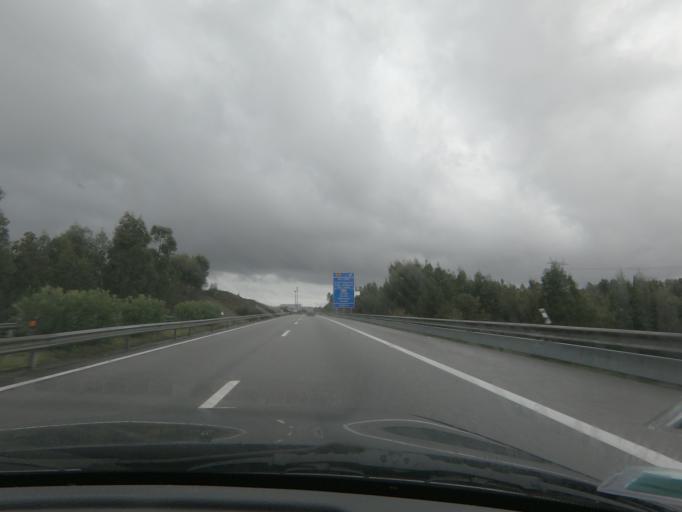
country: PT
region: Porto
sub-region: Paredes
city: Recarei
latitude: 41.1746
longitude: -8.4229
